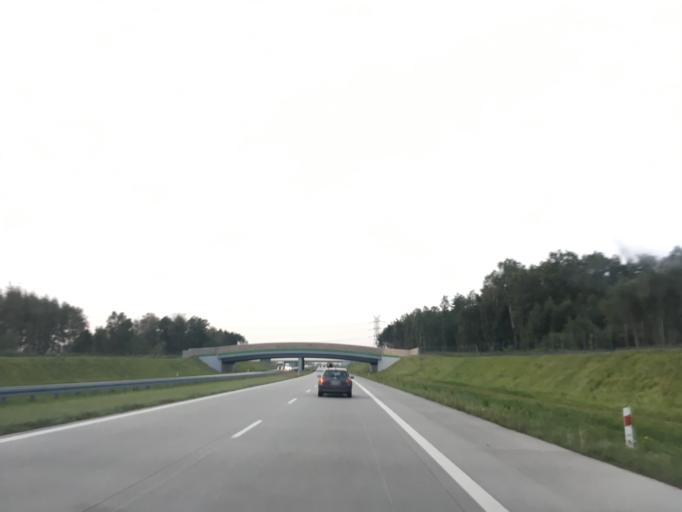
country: PL
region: Lodz Voivodeship
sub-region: Powiat lodzki wschodni
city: Tuszyn
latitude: 51.6071
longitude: 19.5748
